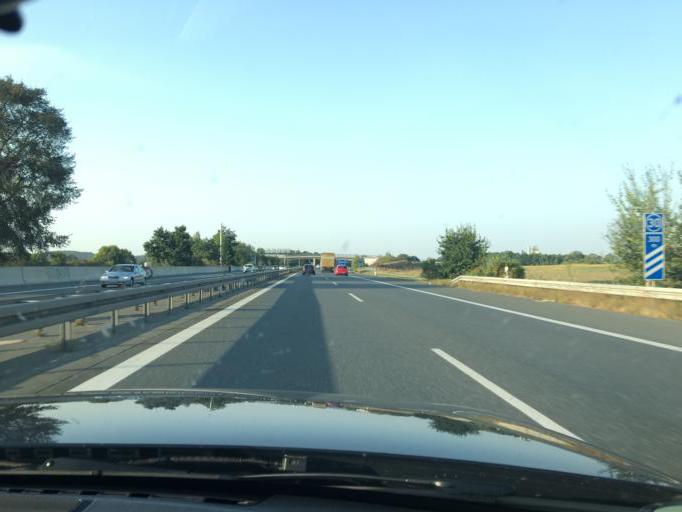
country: DE
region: Bavaria
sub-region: Regierungsbezirk Mittelfranken
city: Bubenreuth
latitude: 49.6300
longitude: 11.0086
